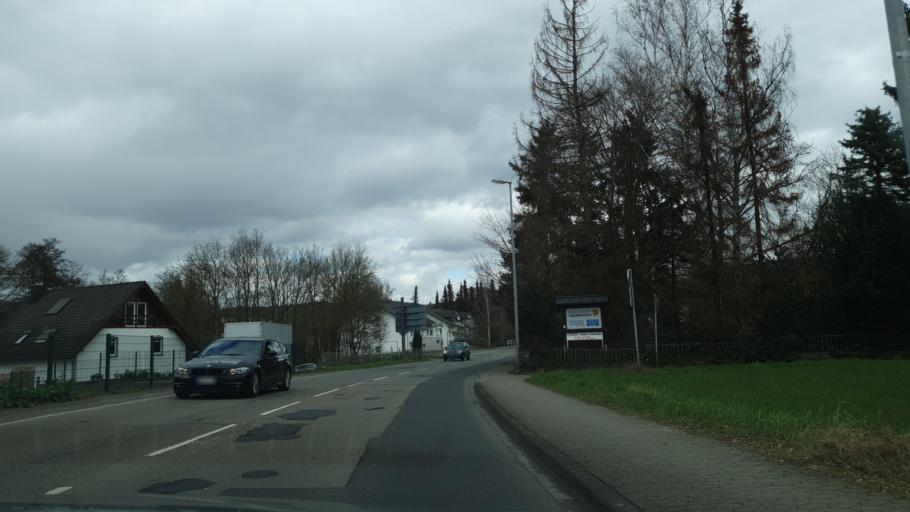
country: DE
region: Rheinland-Pfalz
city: Melsbach
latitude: 50.4676
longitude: 7.4884
